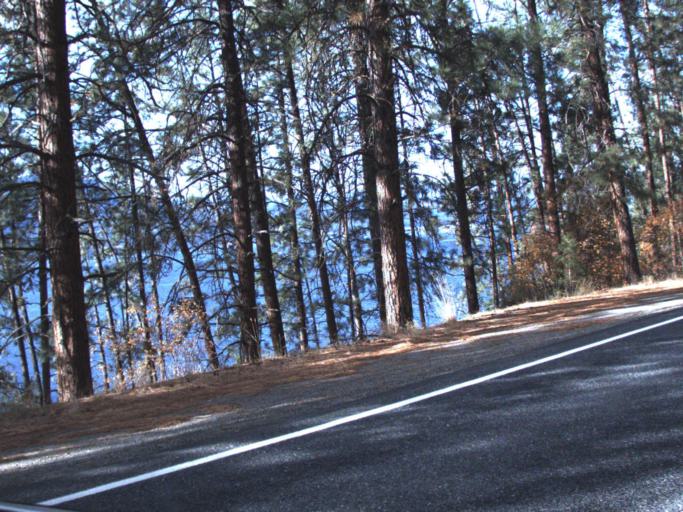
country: US
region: Washington
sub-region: Stevens County
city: Kettle Falls
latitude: 48.3133
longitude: -118.1486
